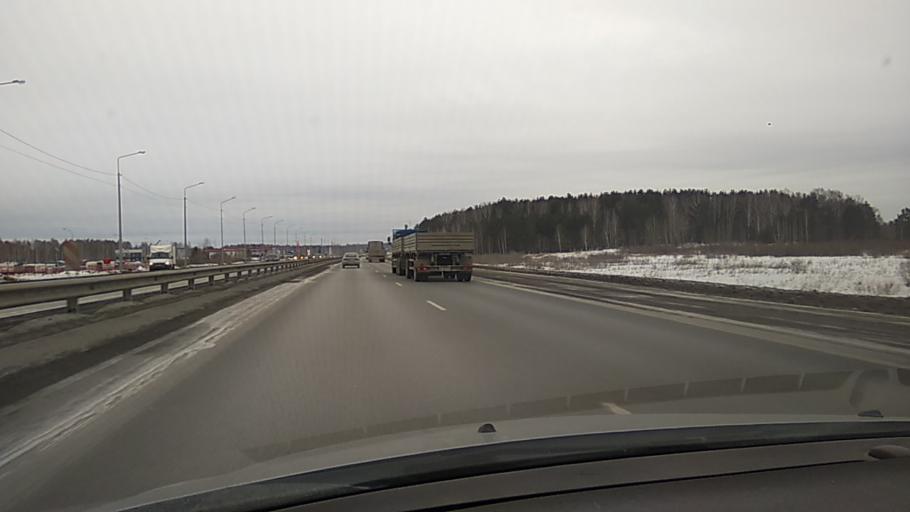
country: RU
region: Sverdlovsk
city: Severka
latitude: 56.8387
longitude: 60.1715
